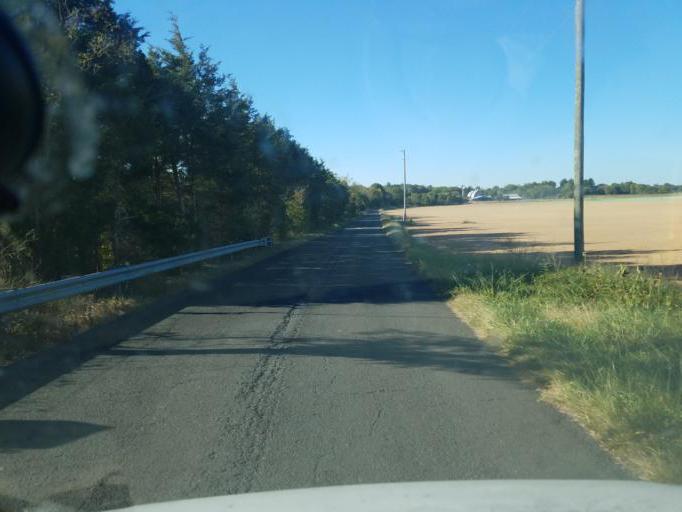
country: US
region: Virginia
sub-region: Fauquier County
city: Bealeton
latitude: 38.5413
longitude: -77.8132
